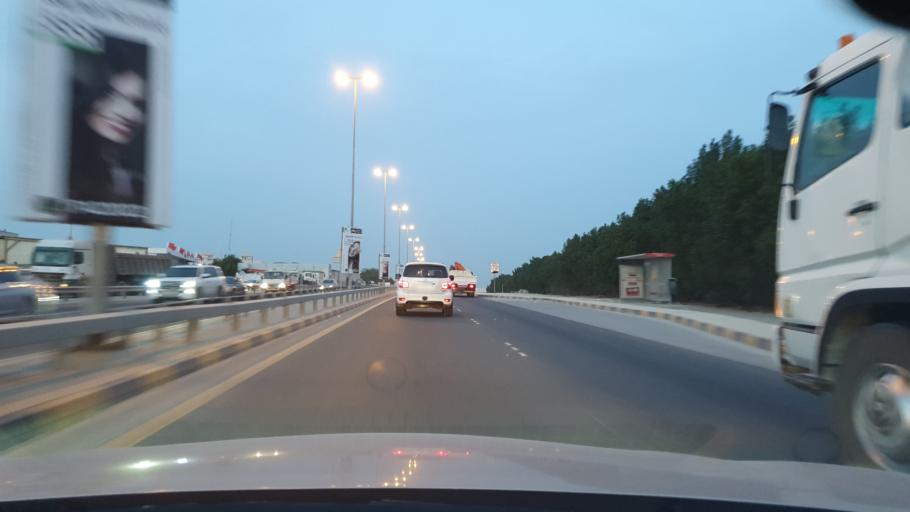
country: BH
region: Northern
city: Ar Rifa'
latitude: 26.1153
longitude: 50.5794
